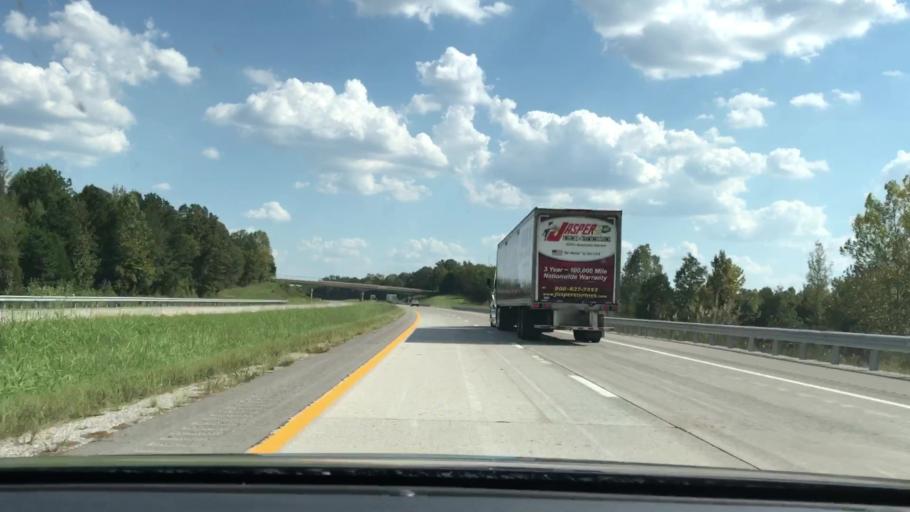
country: US
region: Kentucky
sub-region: Ohio County
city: Oak Grove
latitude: 37.3533
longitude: -86.7874
